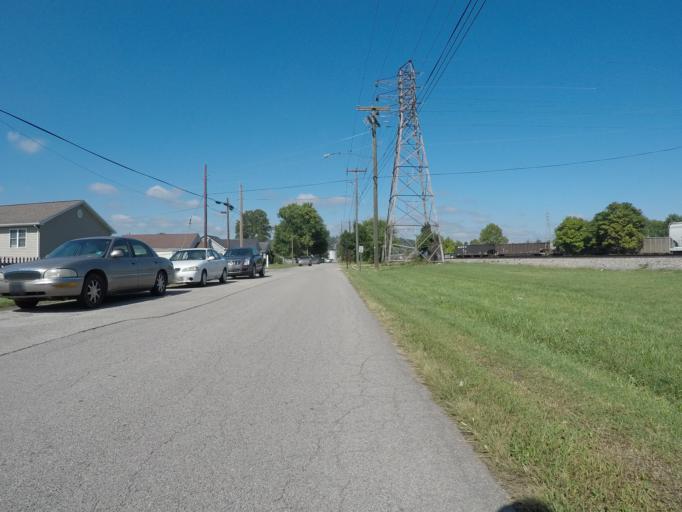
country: US
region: West Virginia
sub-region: Wayne County
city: Kenova
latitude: 38.4049
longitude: -82.5829
